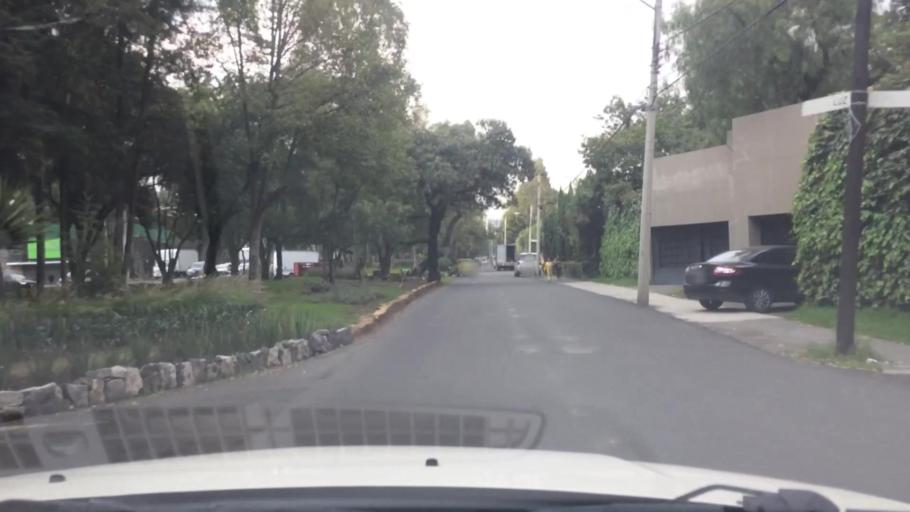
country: MX
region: Mexico City
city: Magdalena Contreras
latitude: 19.3102
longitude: -99.2097
